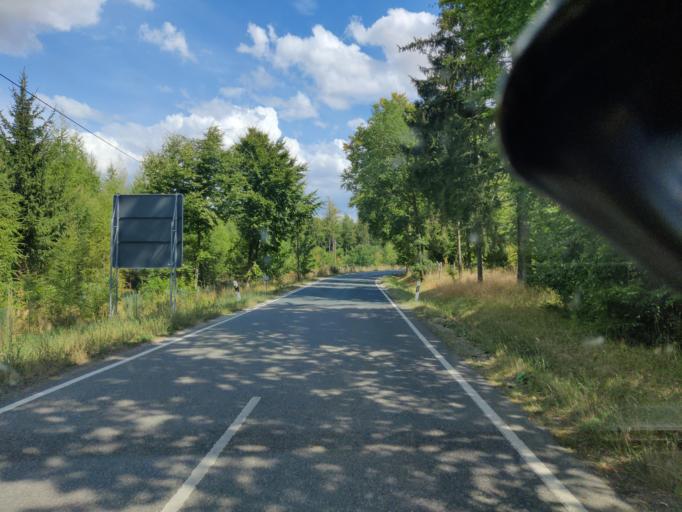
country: DE
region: Bavaria
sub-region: Regierungsbezirk Mittelfranken
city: Thalmassing
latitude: 49.0734
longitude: 11.2096
